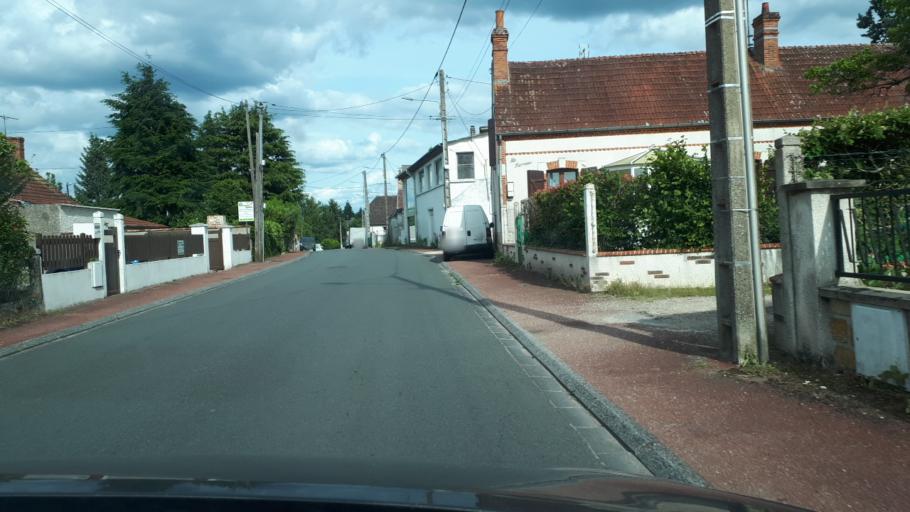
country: FR
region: Centre
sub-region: Departement du Loir-et-Cher
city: Romorantin-Lanthenay
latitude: 47.3516
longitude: 1.7581
